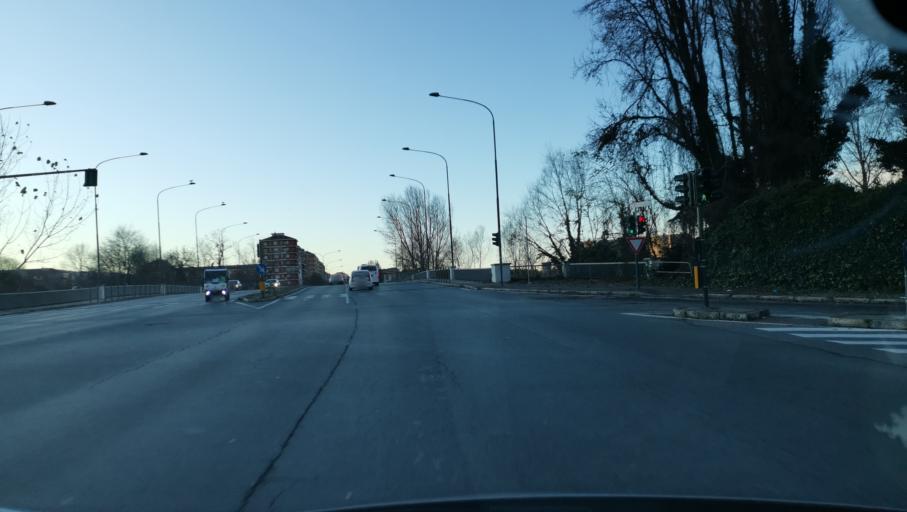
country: IT
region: Piedmont
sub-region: Provincia di Torino
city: Turin
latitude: 45.1149
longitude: 7.6989
